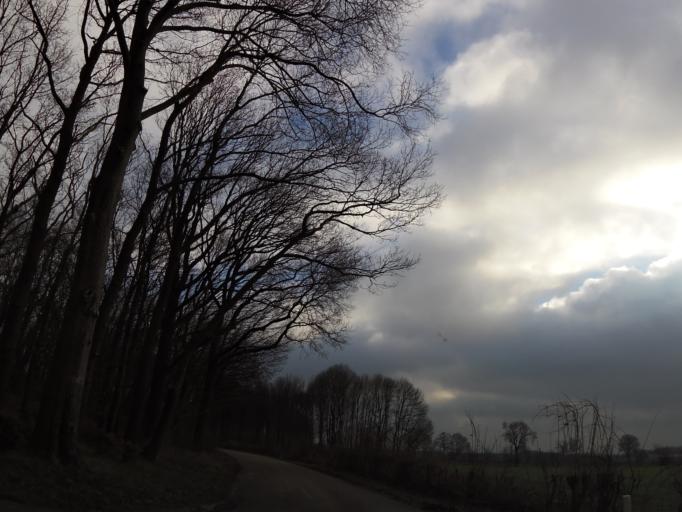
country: NL
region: Limburg
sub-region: Gemeente Bergen
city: Wellerlooi
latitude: 51.5371
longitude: 6.1203
